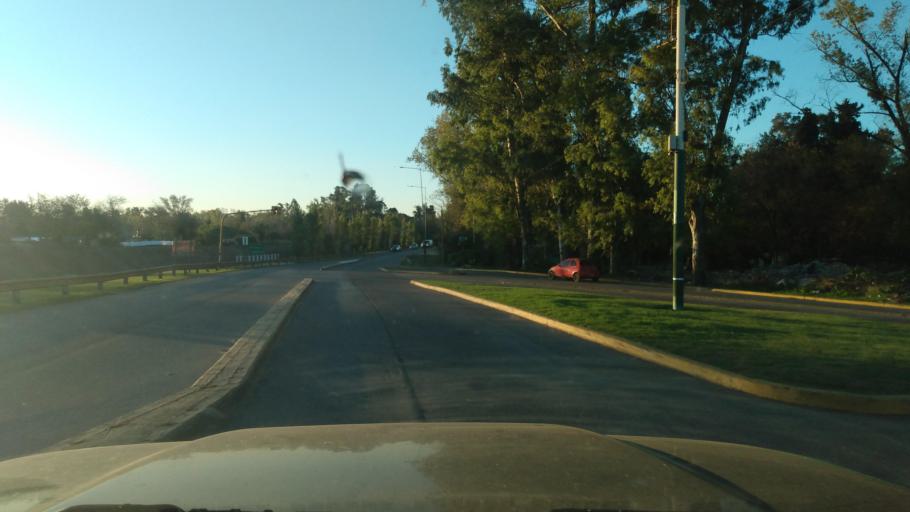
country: AR
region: Buenos Aires
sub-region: Partido de Merlo
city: Merlo
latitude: -34.6407
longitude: -58.7310
